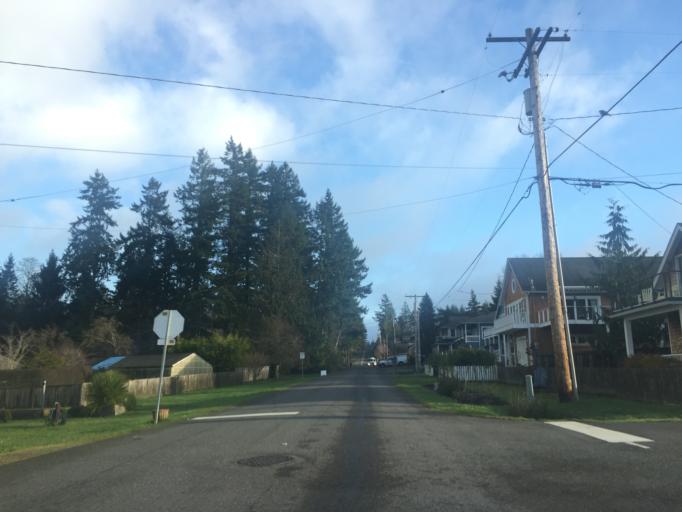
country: US
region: Washington
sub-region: Thurston County
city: Olympia
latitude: 47.1394
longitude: -122.9039
